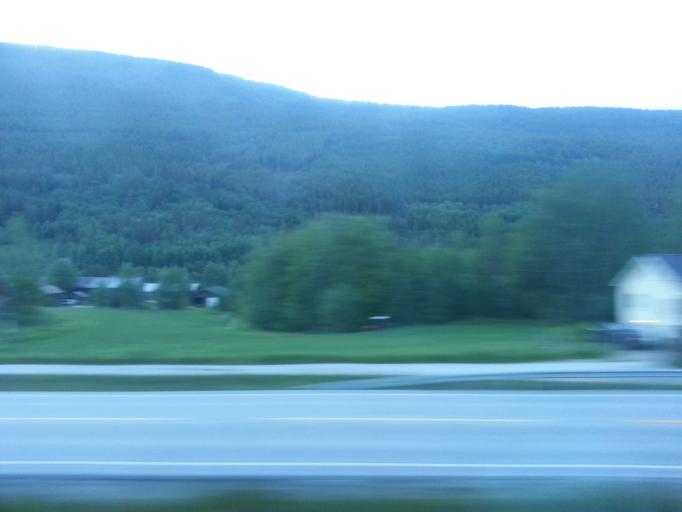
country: NO
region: Oppland
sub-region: Dovre
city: Dovre
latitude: 61.9145
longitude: 9.3571
